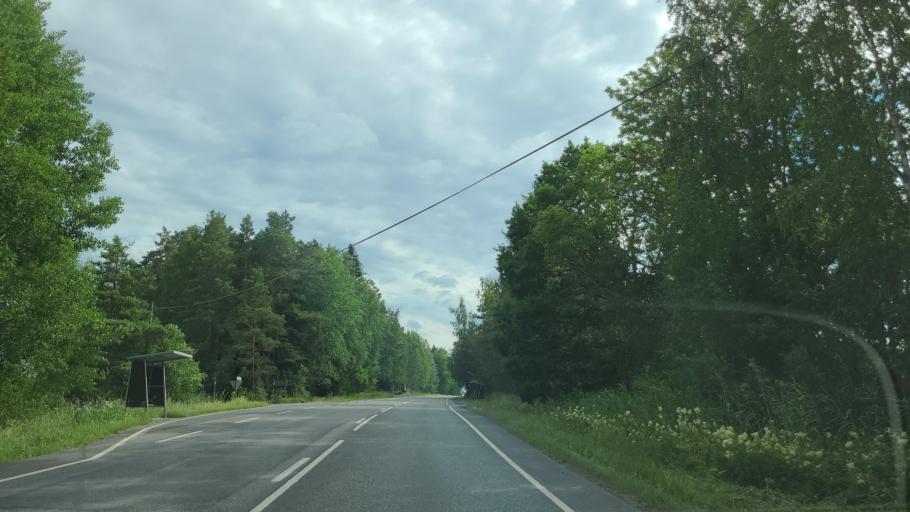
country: FI
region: Varsinais-Suomi
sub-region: Turku
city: Merimasku
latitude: 60.4408
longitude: 21.8975
